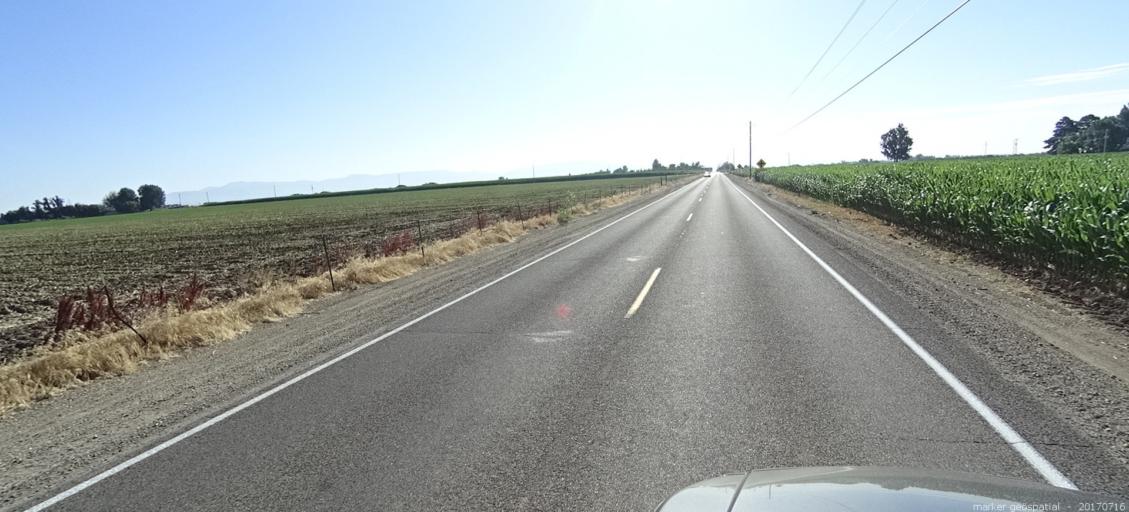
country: US
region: Idaho
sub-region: Ada County
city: Meridian
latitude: 43.5464
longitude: -116.3786
